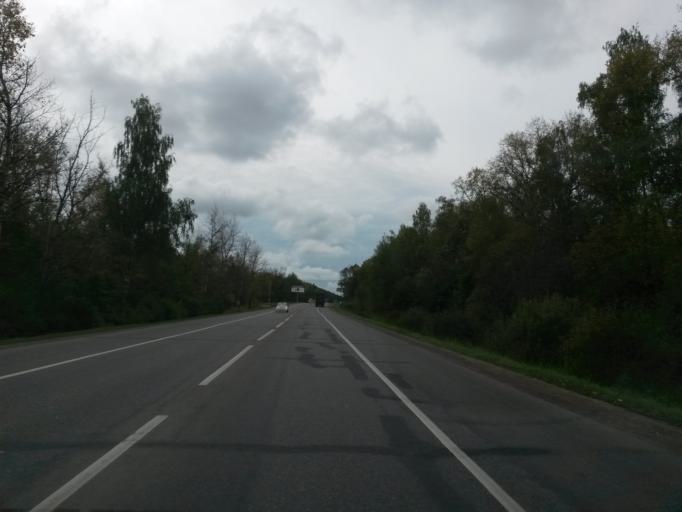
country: RU
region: Moskovskaya
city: Stolbovaya
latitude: 55.2024
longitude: 37.5071
